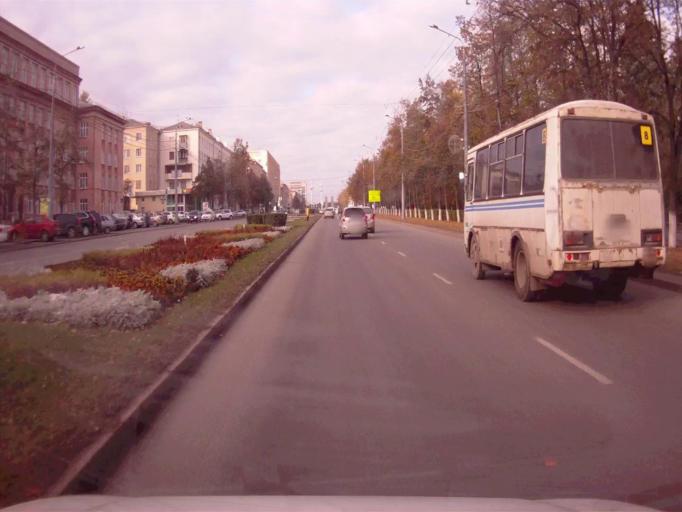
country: RU
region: Chelyabinsk
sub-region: Gorod Chelyabinsk
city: Chelyabinsk
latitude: 55.1598
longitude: 61.3792
